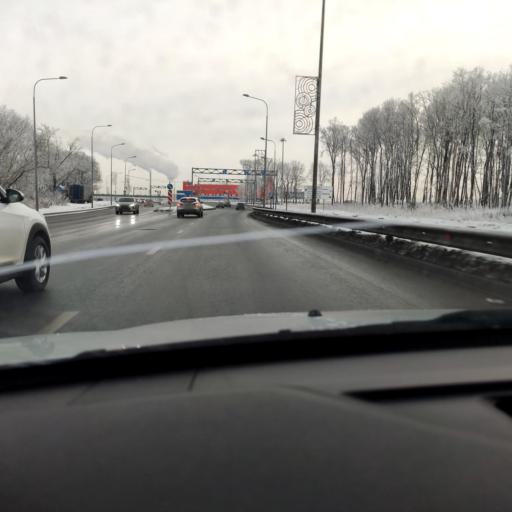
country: RU
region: Samara
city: Petra-Dubrava
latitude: 53.2810
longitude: 50.2527
